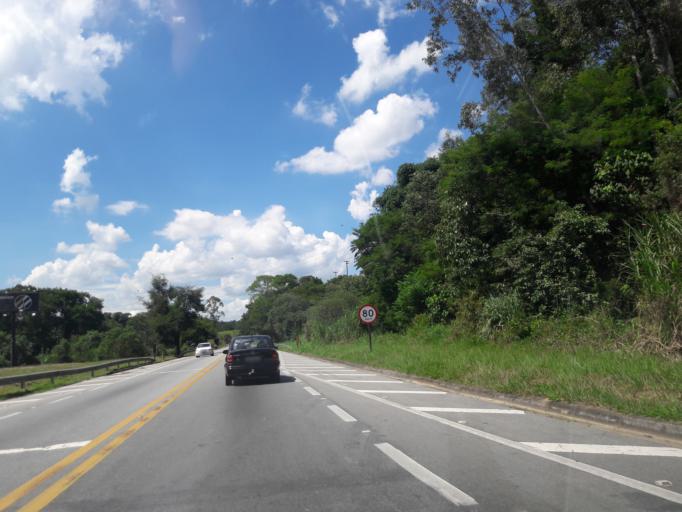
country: BR
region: Sao Paulo
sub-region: Cajamar
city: Cajamar
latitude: -23.3121
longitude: -46.8172
